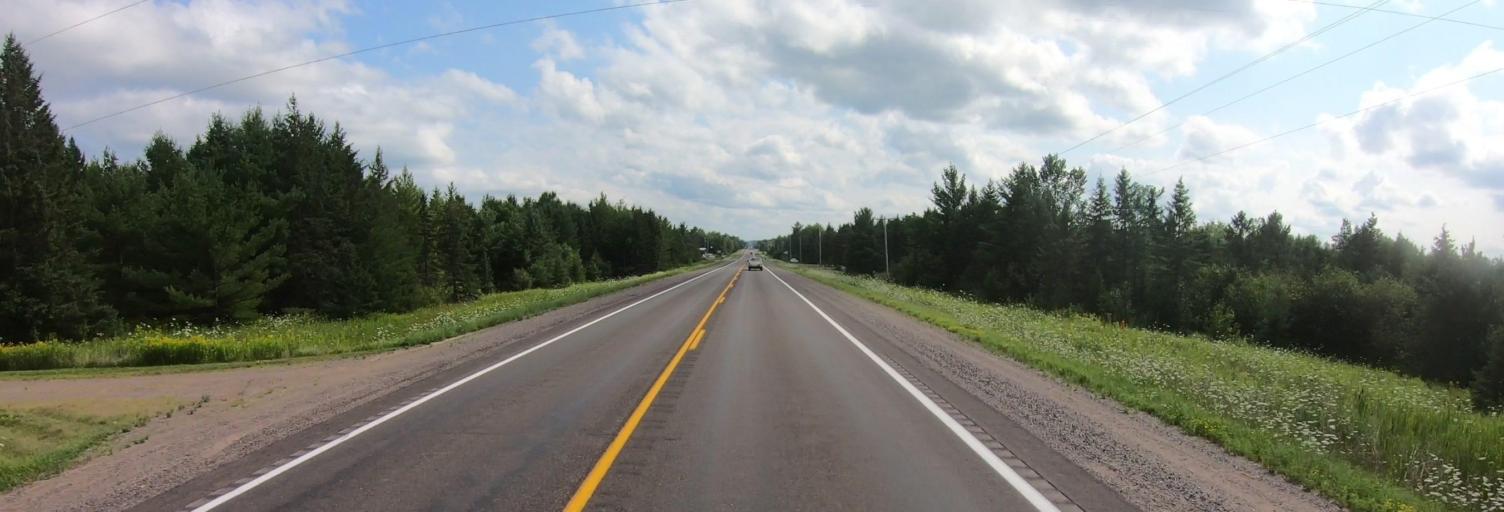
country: US
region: Michigan
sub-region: Ontonagon County
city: Ontonagon
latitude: 46.5524
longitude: -89.1787
